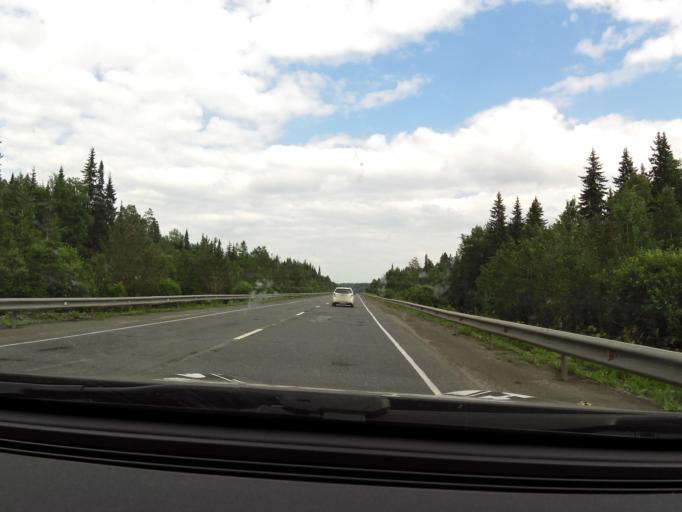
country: RU
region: Sverdlovsk
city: Druzhinino
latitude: 56.7964
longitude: 59.4280
